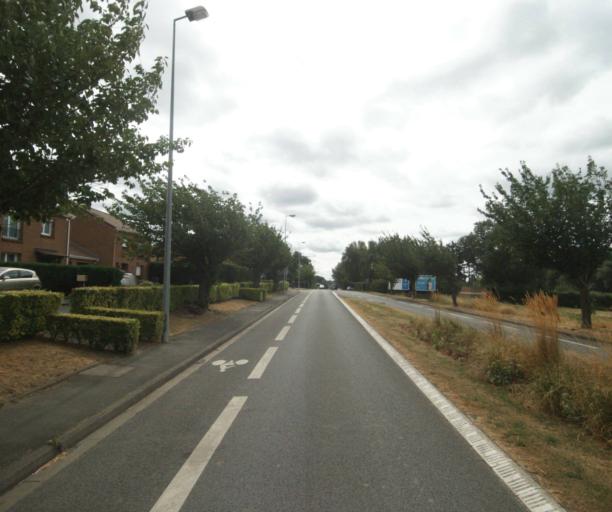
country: FR
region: Nord-Pas-de-Calais
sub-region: Departement du Nord
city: Linselles
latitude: 50.7328
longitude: 3.0888
